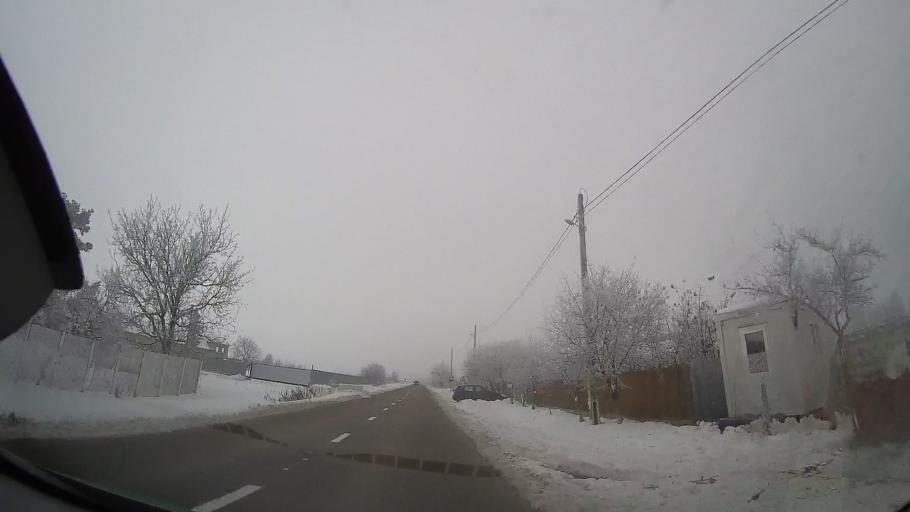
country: RO
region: Neamt
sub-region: Comuna Horia
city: Cotu Vames
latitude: 46.8890
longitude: 26.9664
